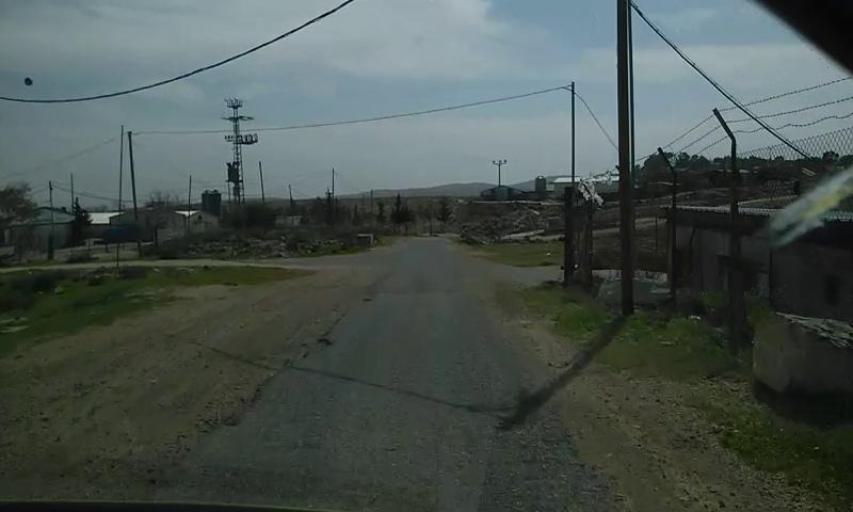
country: PS
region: West Bank
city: Khallat al Mayyah
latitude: 31.4352
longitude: 35.1885
